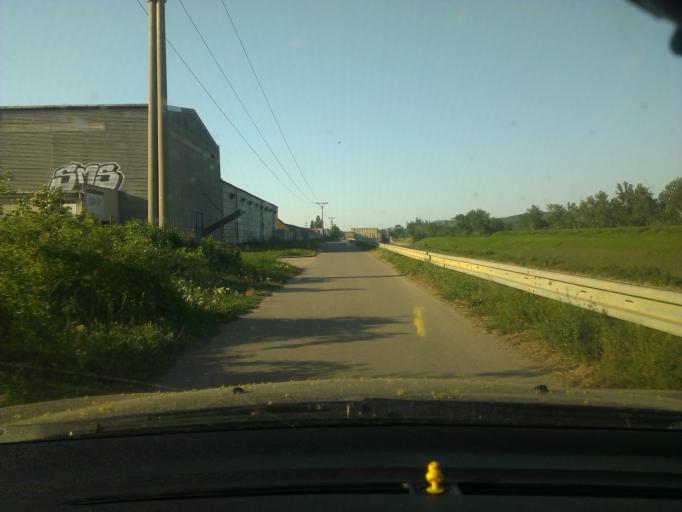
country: SK
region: Trnavsky
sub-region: Okres Trnava
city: Piestany
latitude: 48.6533
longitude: 17.8515
